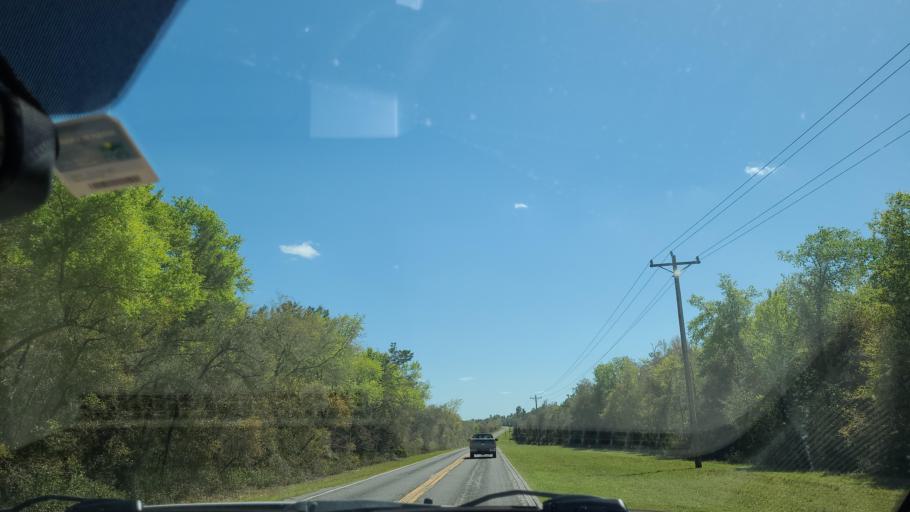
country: US
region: Florida
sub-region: Marion County
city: Citra
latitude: 29.3866
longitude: -81.8881
